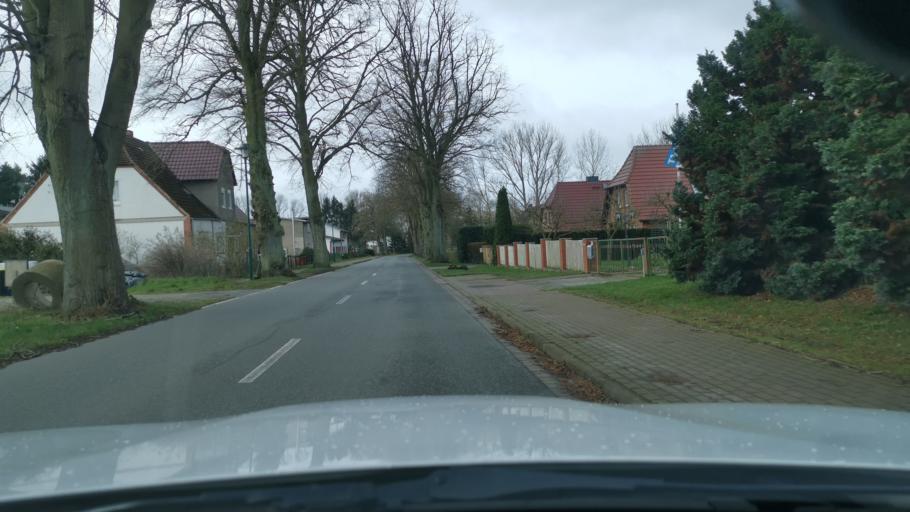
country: DE
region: Mecklenburg-Vorpommern
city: Laage
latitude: 53.9913
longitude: 12.3655
